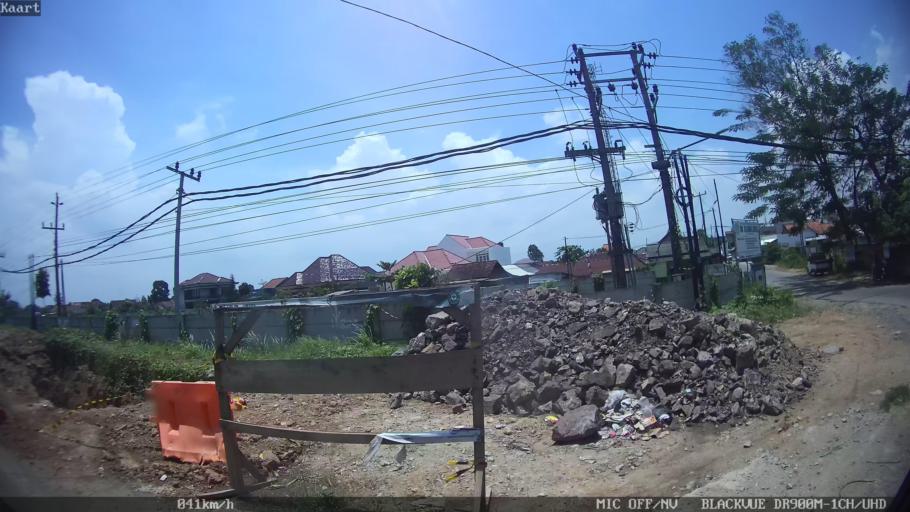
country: ID
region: Lampung
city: Kedaton
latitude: -5.3837
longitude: 105.2868
